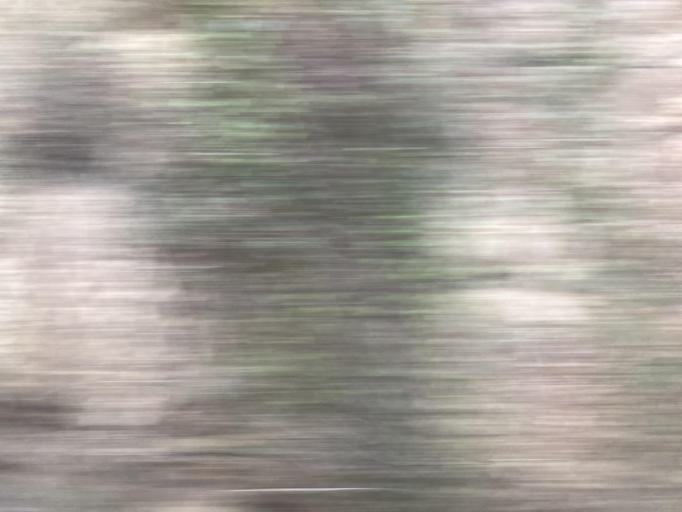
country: ES
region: Catalonia
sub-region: Provincia de Barcelona
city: Vilanova i la Geltru
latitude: 41.2199
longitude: 1.7621
